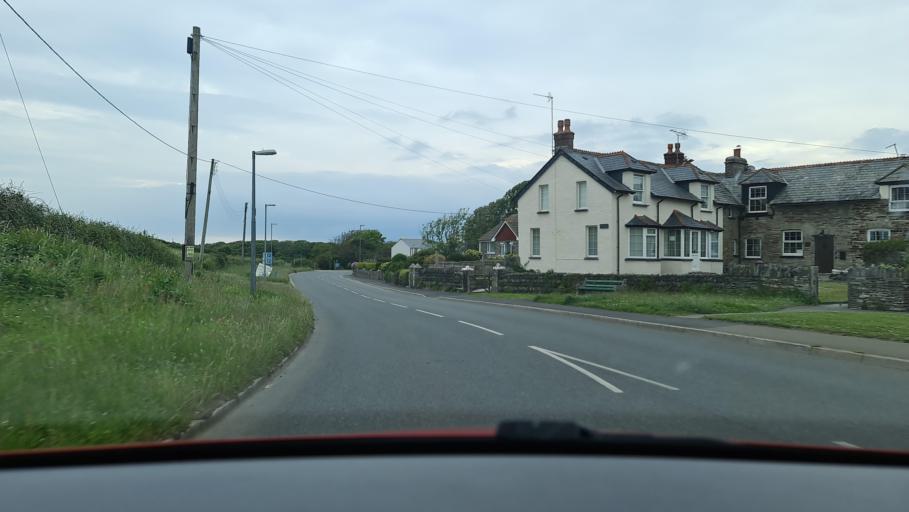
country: GB
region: England
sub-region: Cornwall
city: Tintagel
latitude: 50.6601
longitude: -4.7495
